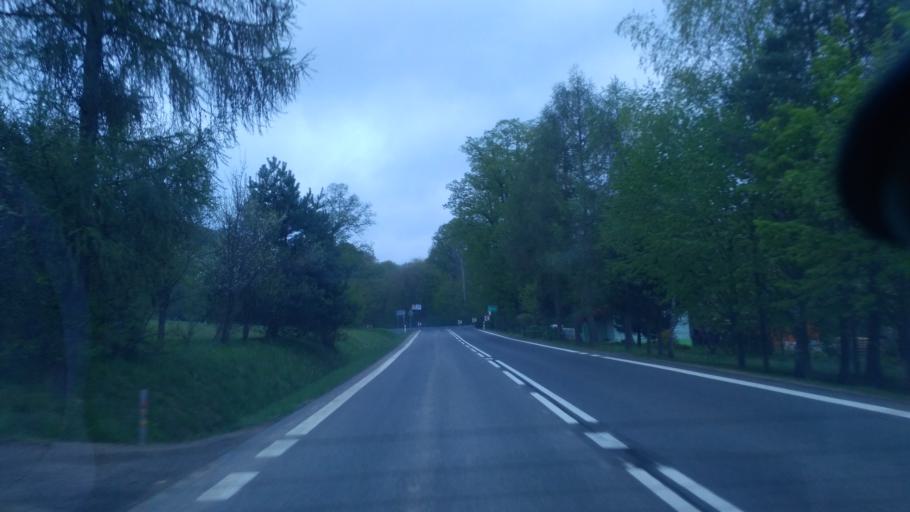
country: PL
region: Subcarpathian Voivodeship
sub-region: Powiat sanocki
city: Tyrawa Woloska
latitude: 49.5474
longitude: 22.3193
